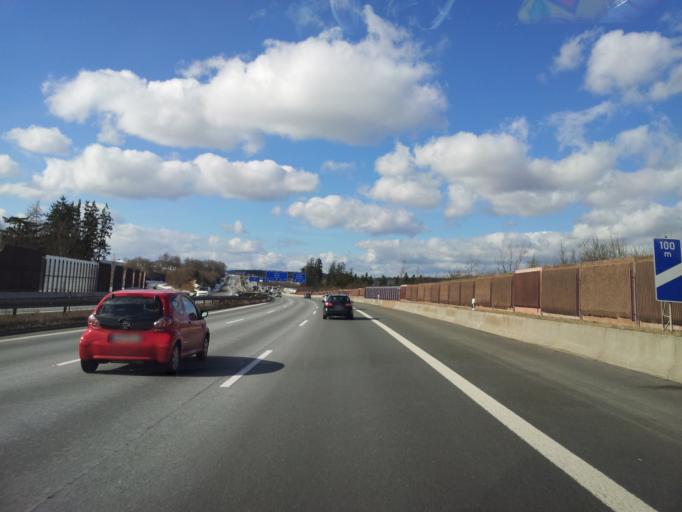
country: DE
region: Bavaria
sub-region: Upper Franconia
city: Leupoldsgrun
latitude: 50.3162
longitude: 11.7992
